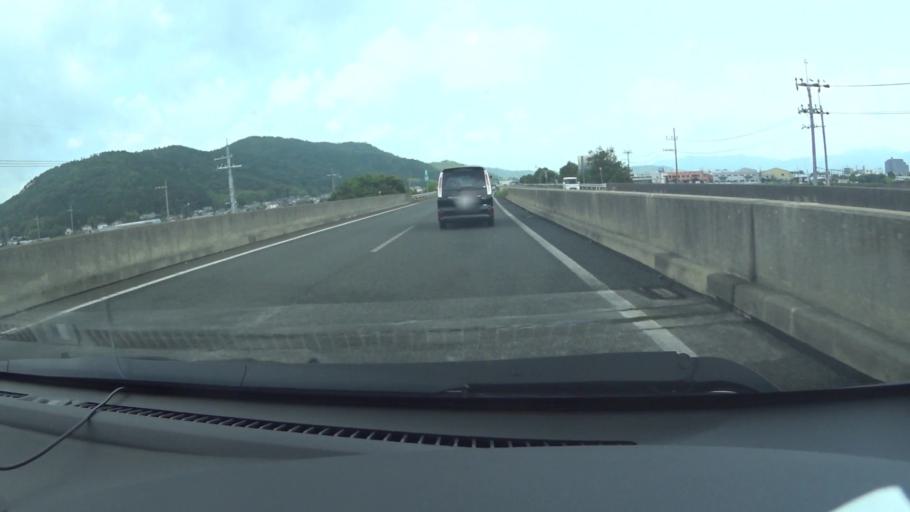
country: JP
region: Kyoto
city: Kameoka
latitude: 35.0235
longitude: 135.5494
